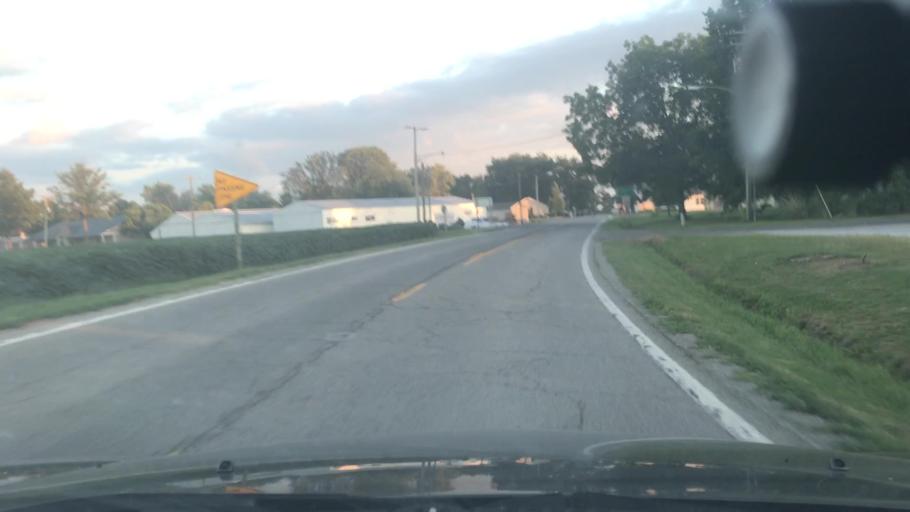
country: US
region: Illinois
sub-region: Washington County
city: Okawville
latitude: 38.3942
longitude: -89.4924
